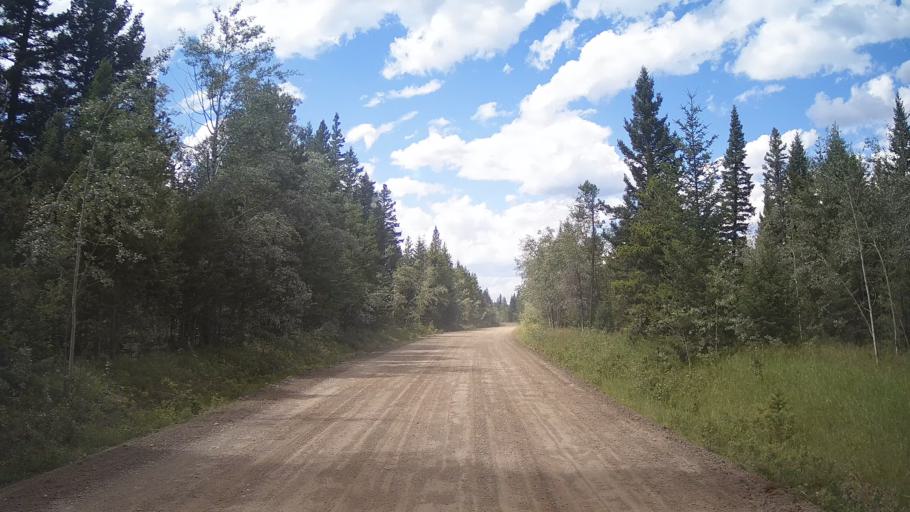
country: CA
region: British Columbia
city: Lillooet
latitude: 51.3270
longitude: -121.8836
